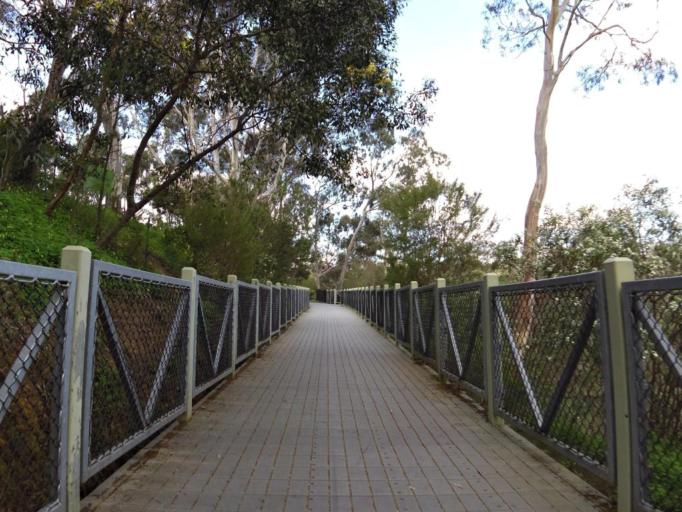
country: AU
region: Victoria
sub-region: Banyule
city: Darch
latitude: -37.7521
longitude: 145.1184
